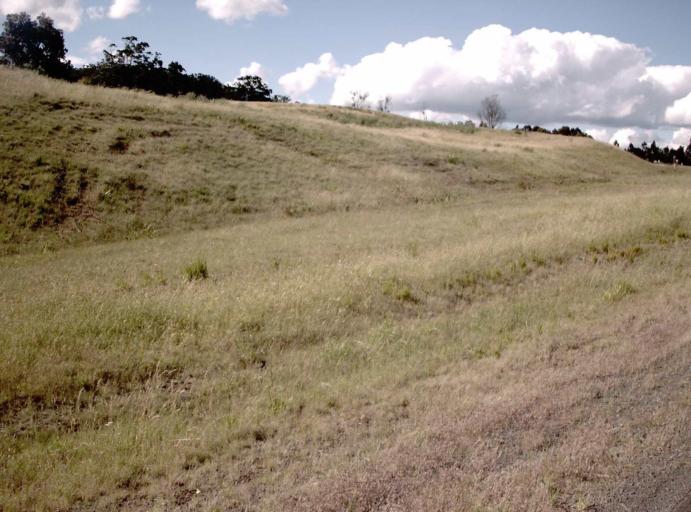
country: AU
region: Victoria
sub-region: Latrobe
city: Moe
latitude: -38.1913
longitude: 146.3292
